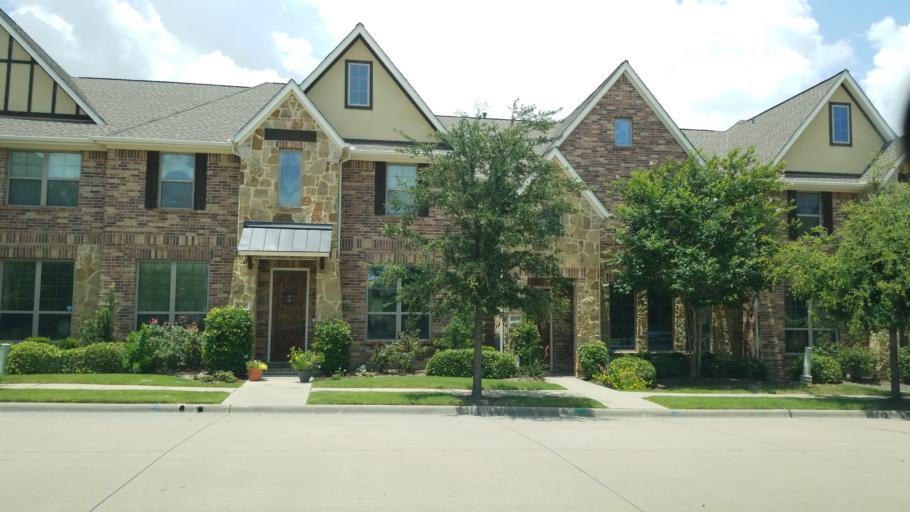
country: US
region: Texas
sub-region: Dallas County
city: Coppell
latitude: 32.9485
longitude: -96.9620
